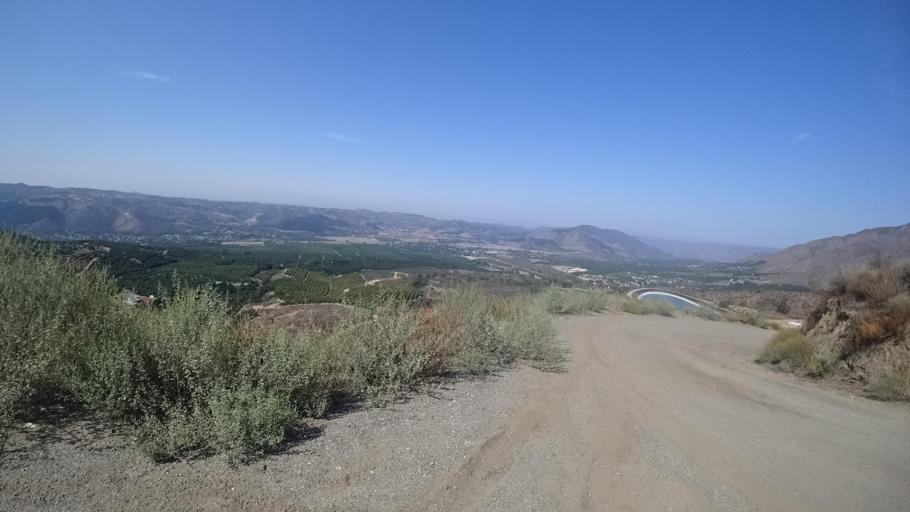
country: US
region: California
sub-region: San Diego County
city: Valley Center
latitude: 33.3257
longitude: -116.9640
